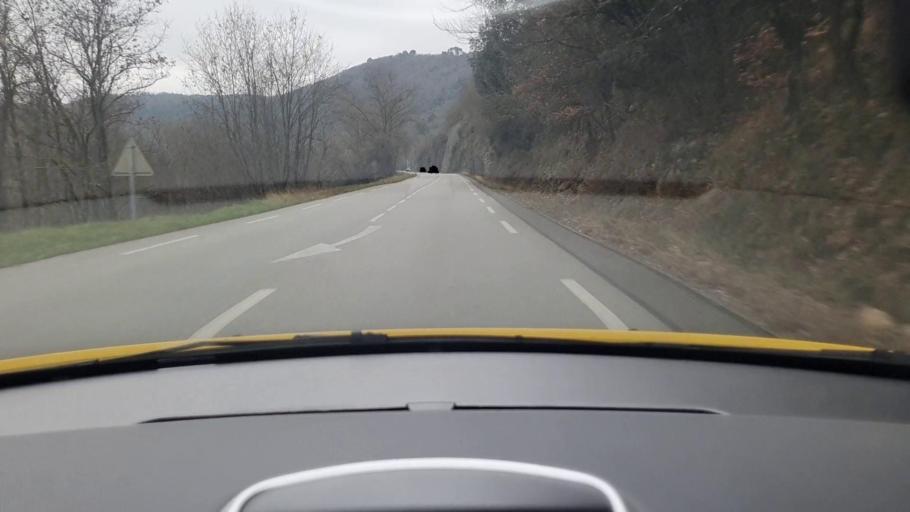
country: FR
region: Languedoc-Roussillon
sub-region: Departement du Gard
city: Molieres-sur-Ceze
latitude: 44.2702
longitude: 4.1544
